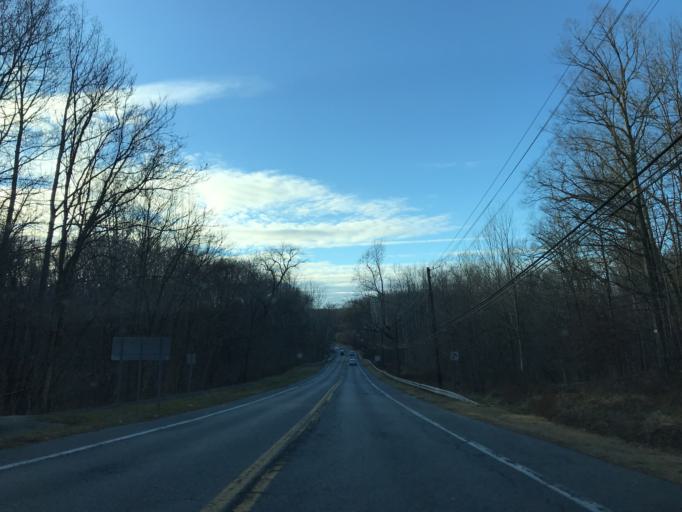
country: US
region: Maryland
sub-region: Montgomery County
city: Fairland
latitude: 39.0767
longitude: -76.9738
